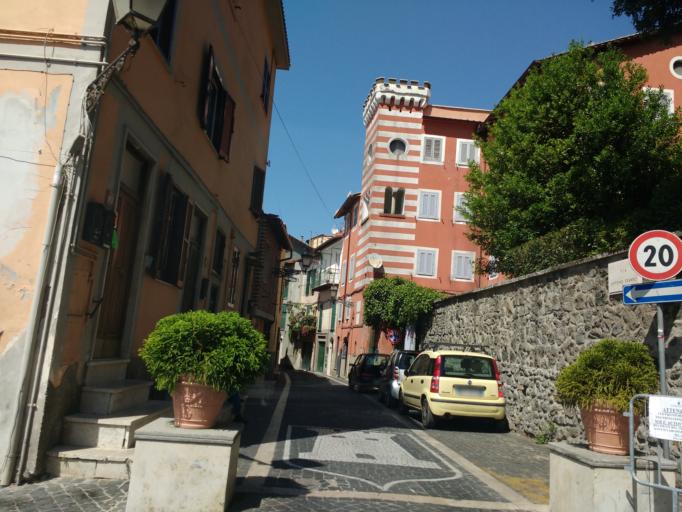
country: IT
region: Latium
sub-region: Citta metropolitana di Roma Capitale
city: Rocca di Papa
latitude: 41.7594
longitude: 12.7087
